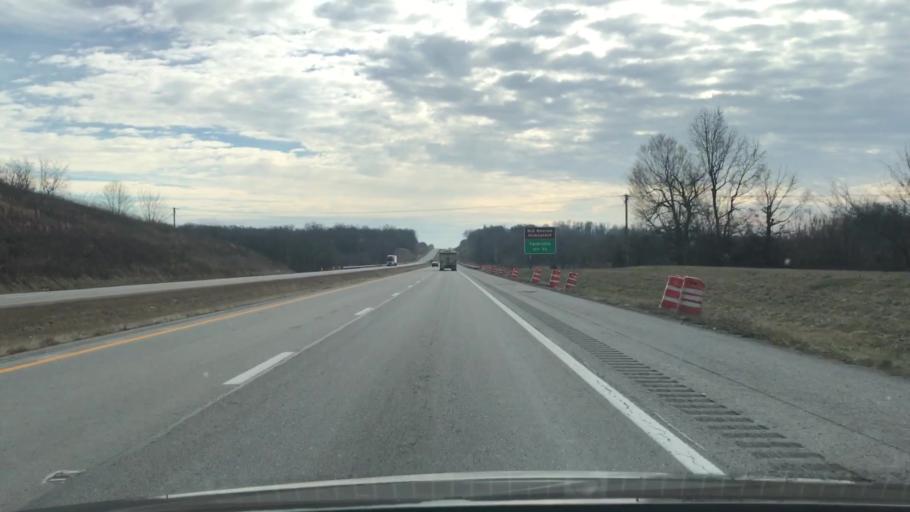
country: US
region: Kentucky
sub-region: Ohio County
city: Hartford
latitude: 37.4805
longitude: -86.9048
